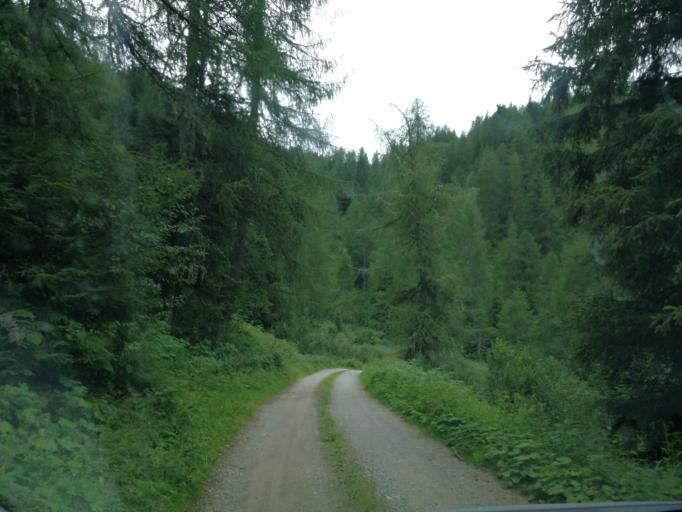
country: IT
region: Trentino-Alto Adige
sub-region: Provincia di Trento
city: Castel Condino
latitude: 45.9386
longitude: 10.5613
